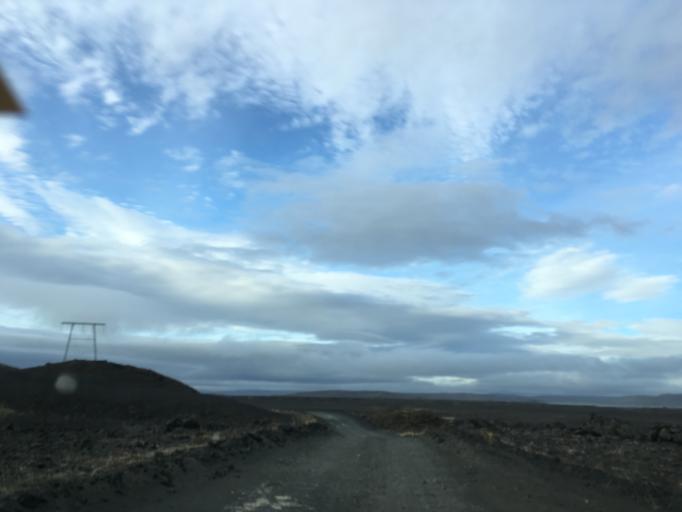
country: IS
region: South
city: Vestmannaeyjar
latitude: 64.1247
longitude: -19.1187
